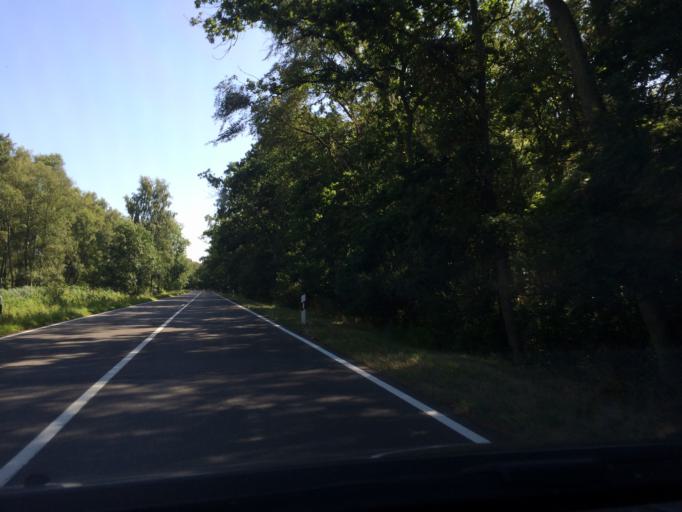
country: DE
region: Mecklenburg-Vorpommern
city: Zingst
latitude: 54.4251
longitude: 12.6510
